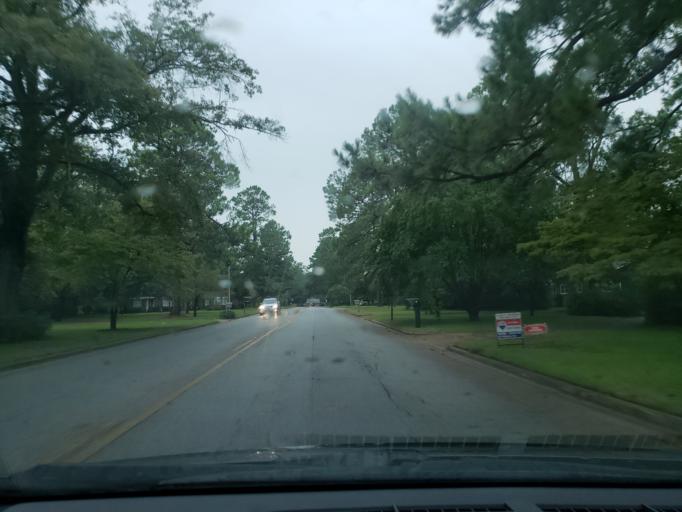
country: US
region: Georgia
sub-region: Dougherty County
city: Albany
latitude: 31.6050
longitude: -84.1906
